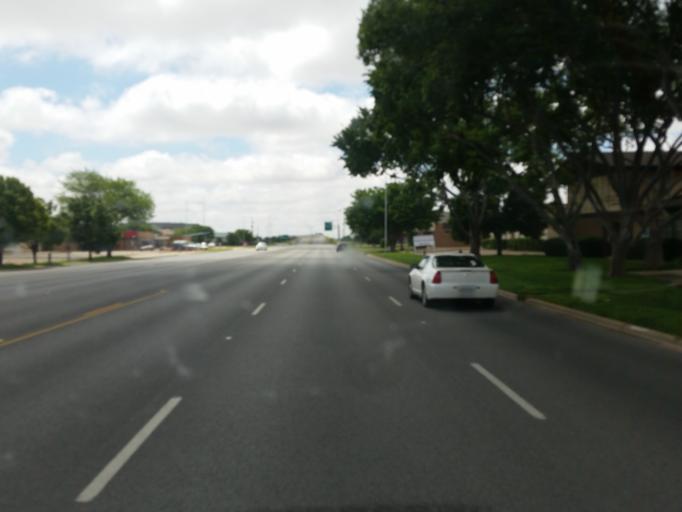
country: US
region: Texas
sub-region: Lubbock County
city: Lubbock
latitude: 33.5436
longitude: -101.8512
